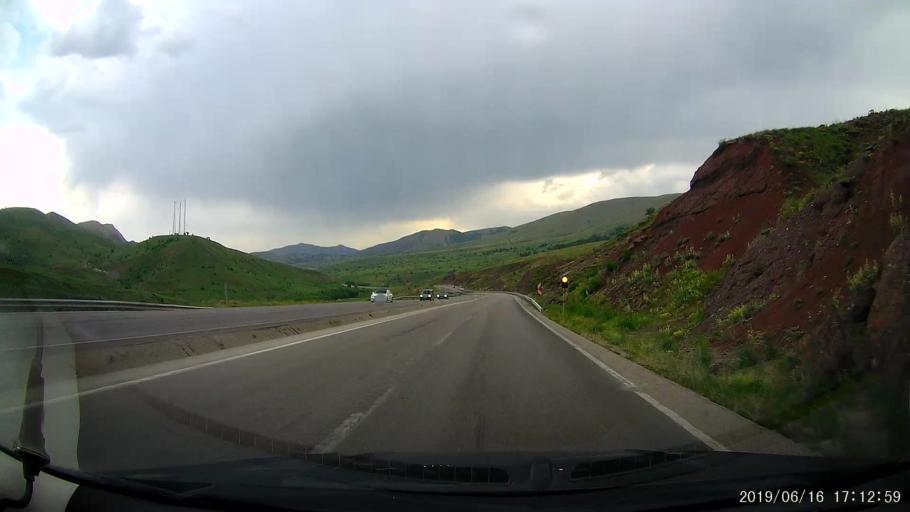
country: TR
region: Erzurum
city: Askale
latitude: 39.8595
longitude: 40.6086
